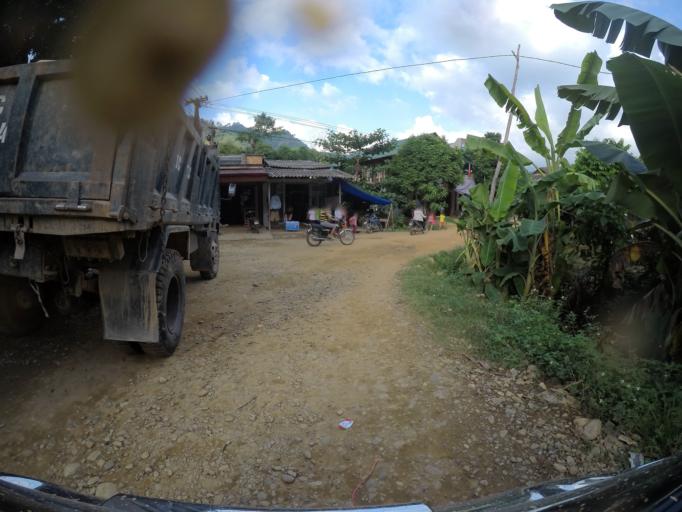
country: VN
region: Yen Bai
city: Son Thinh
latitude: 21.6822
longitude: 104.6102
